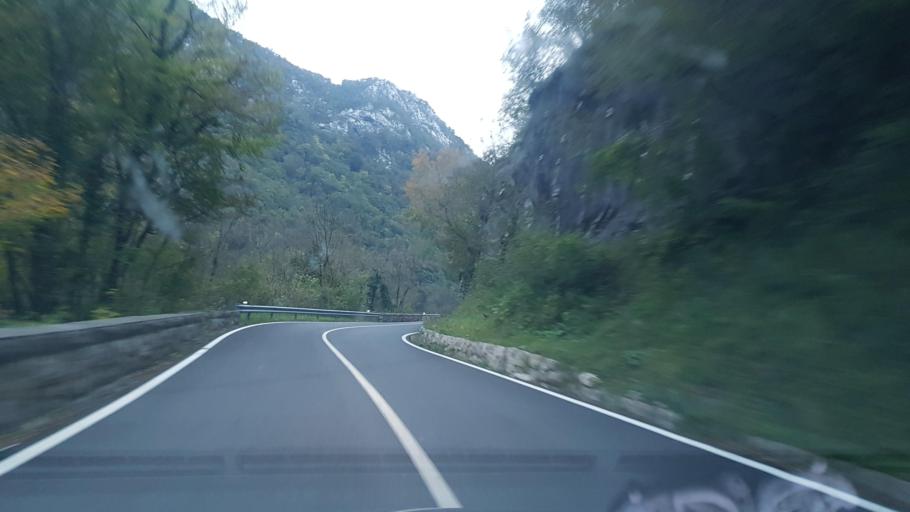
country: IT
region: Friuli Venezia Giulia
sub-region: Provincia di Pordenone
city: Anduins
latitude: 46.2551
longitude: 12.9754
